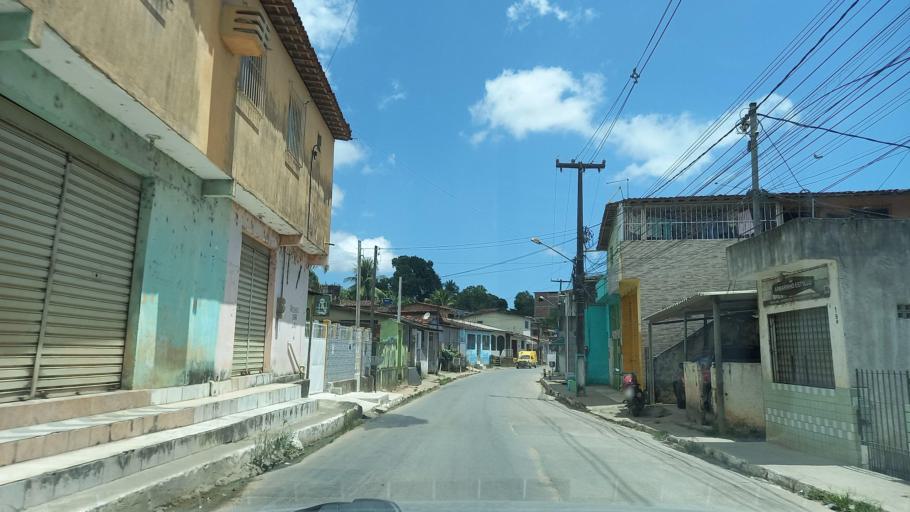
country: BR
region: Pernambuco
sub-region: Jaboatao Dos Guararapes
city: Jaboatao
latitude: -8.1738
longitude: -35.0014
